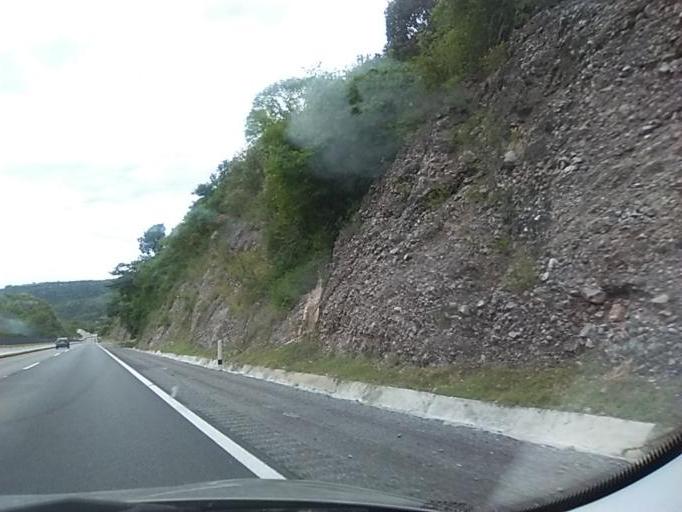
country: MX
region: Guerrero
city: Copalillo
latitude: 18.1221
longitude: -99.2076
